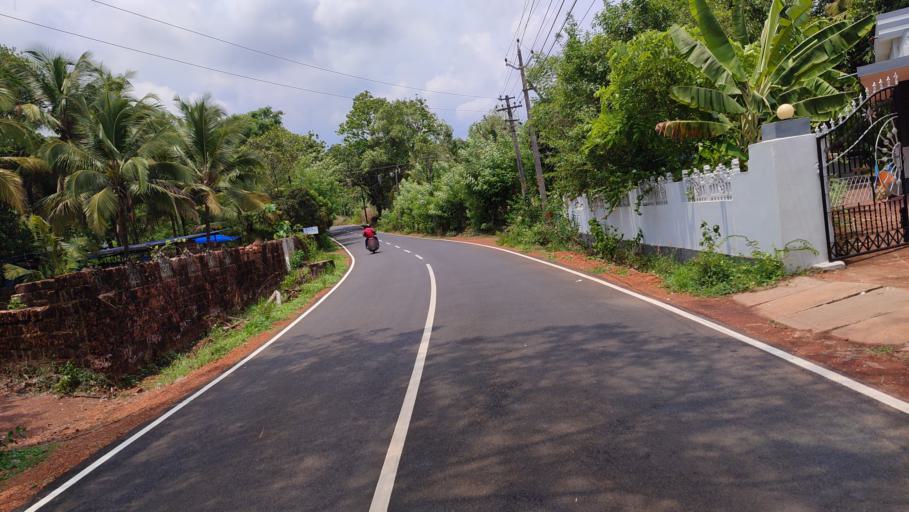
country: IN
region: Kerala
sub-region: Kasaragod District
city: Kannangad
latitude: 12.3195
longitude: 75.1225
